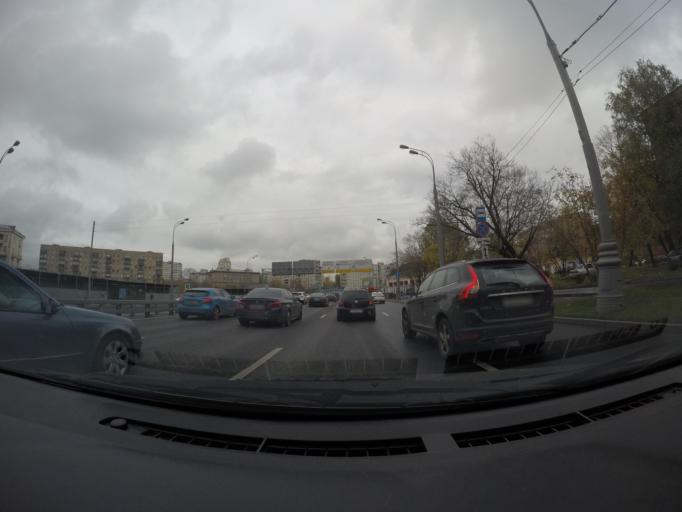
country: RU
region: Moskovskaya
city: Dorogomilovo
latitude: 55.7901
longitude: 37.5716
